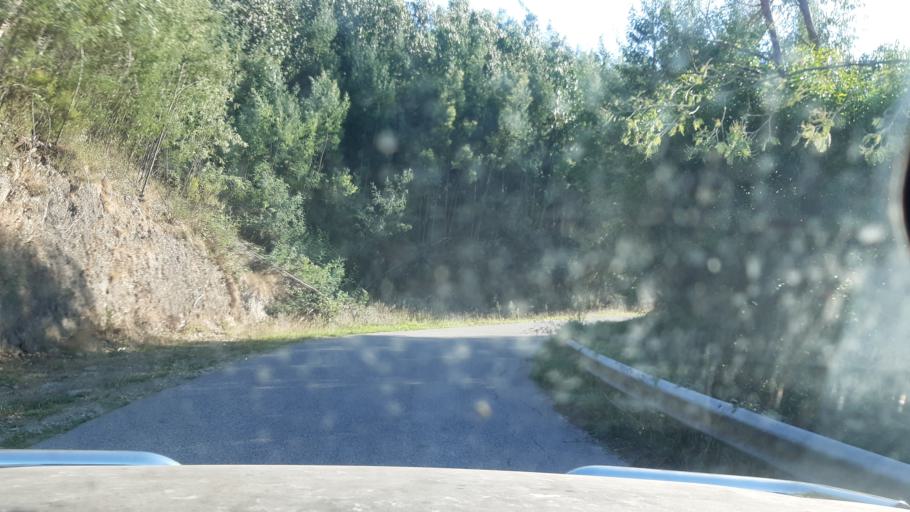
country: PT
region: Aveiro
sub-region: Agueda
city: Aguada de Cima
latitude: 40.5672
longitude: -8.3549
